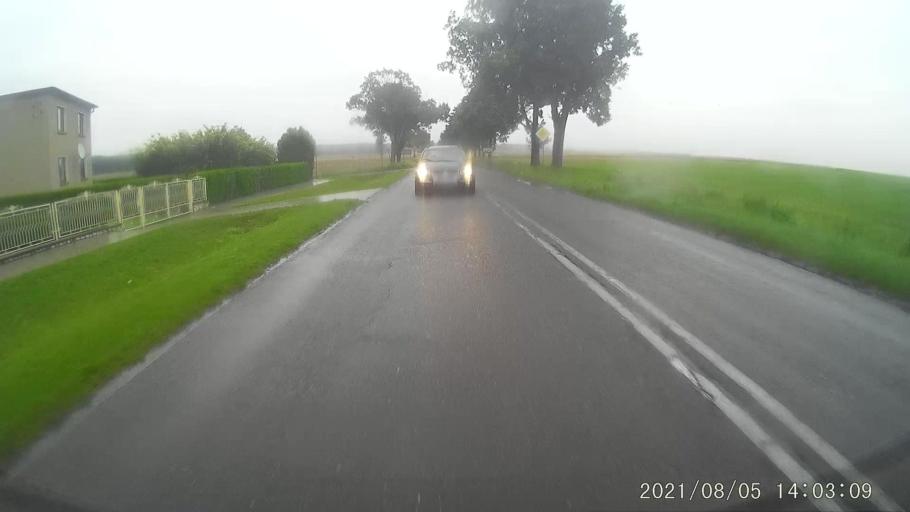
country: PL
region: Opole Voivodeship
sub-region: Powiat krapkowicki
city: Strzeleczki
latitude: 50.4574
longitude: 17.8607
